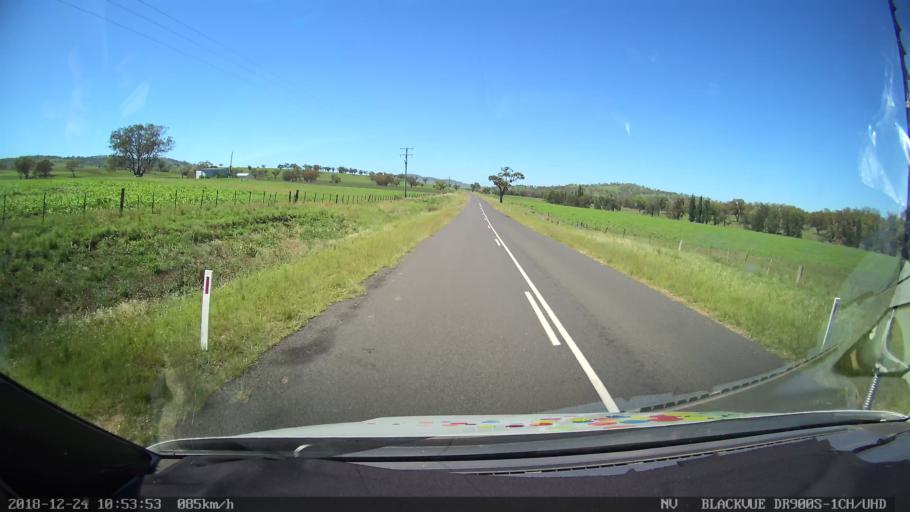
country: AU
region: New South Wales
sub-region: Upper Hunter Shire
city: Merriwa
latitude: -31.9968
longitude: 150.4191
